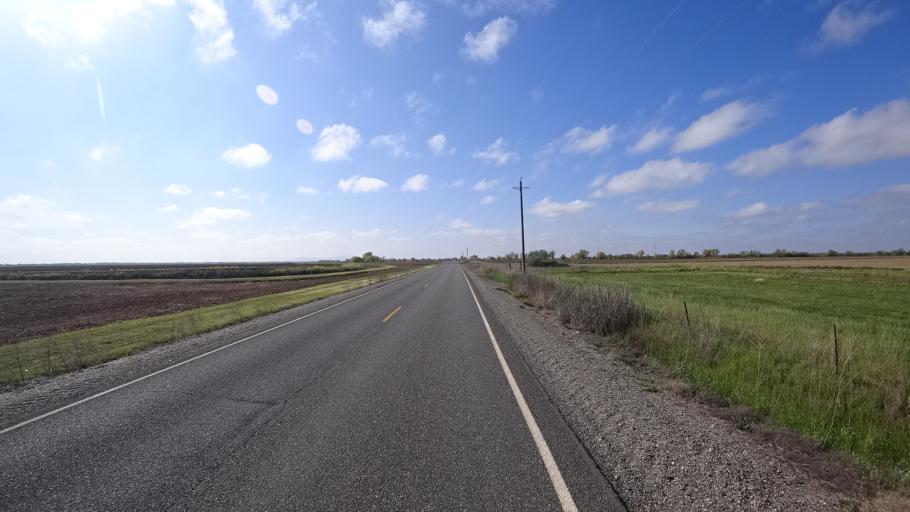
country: US
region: California
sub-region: Butte County
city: Durham
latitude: 39.4908
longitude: -121.9299
